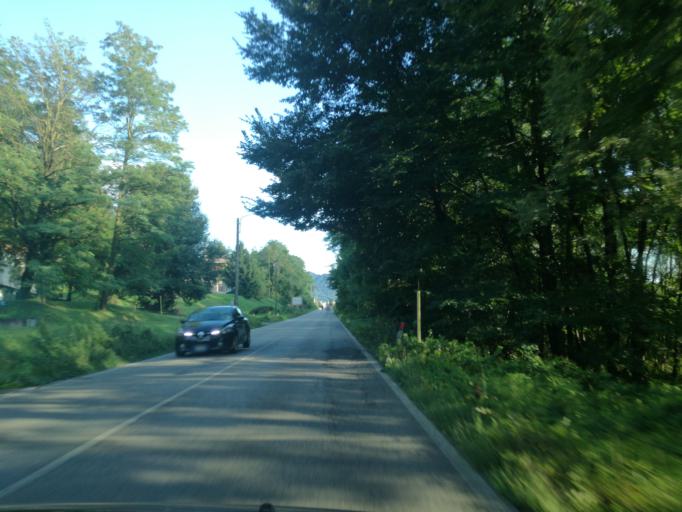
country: IT
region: Lombardy
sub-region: Provincia di Lecco
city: Monte Marenzo
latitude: 45.7699
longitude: 9.4439
